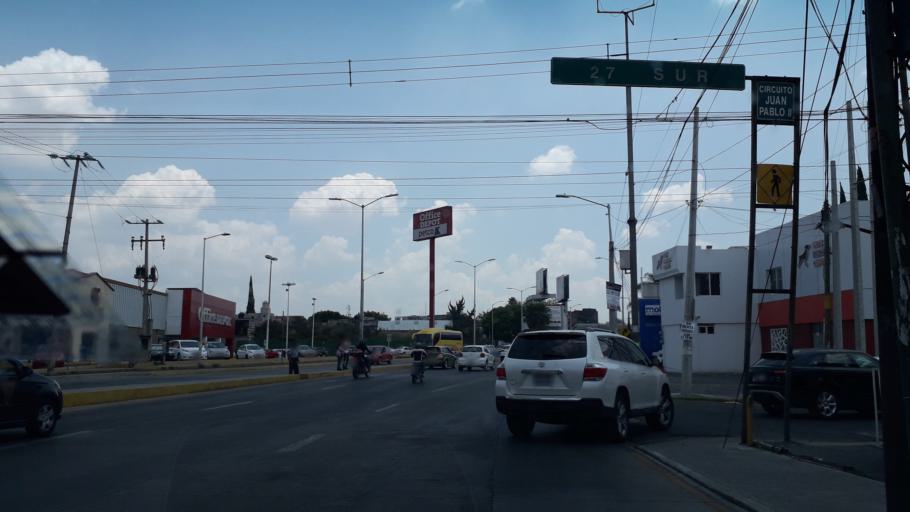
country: MX
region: Puebla
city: Puebla
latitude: 19.0397
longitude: -98.2267
